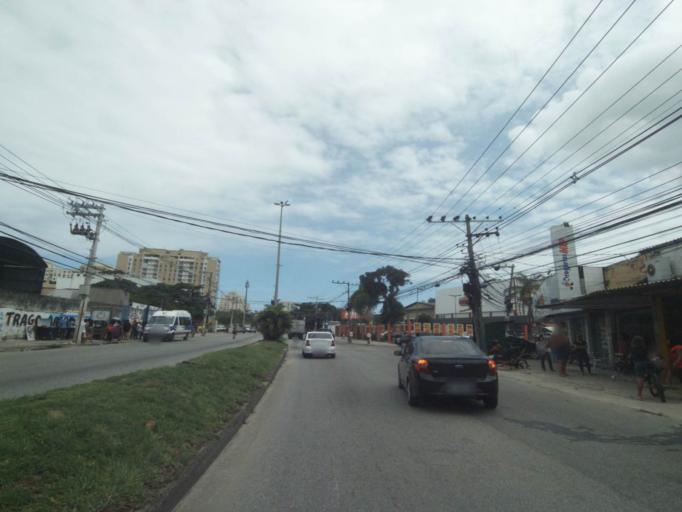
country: BR
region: Rio de Janeiro
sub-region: Nilopolis
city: Nilopolis
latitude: -22.9687
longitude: -43.4135
